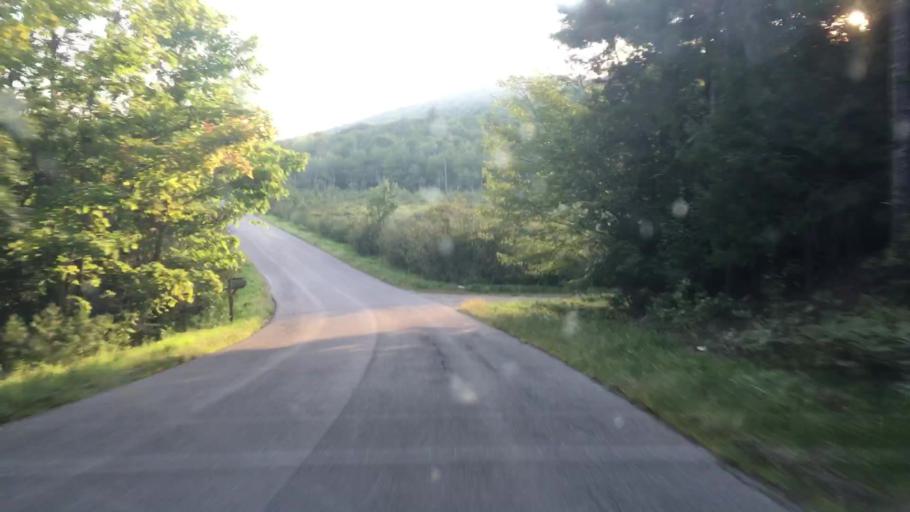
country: US
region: Maine
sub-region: Waldo County
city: Frankfort
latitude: 44.6619
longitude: -68.9296
